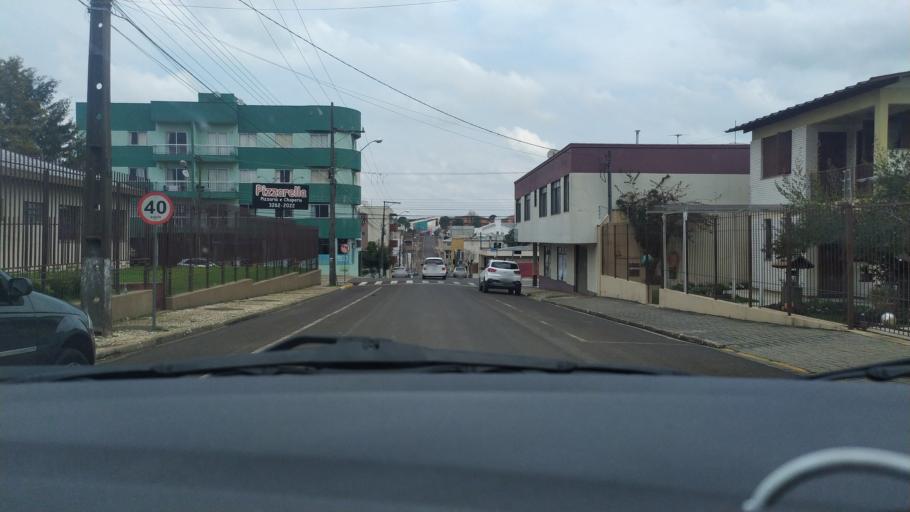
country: BR
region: Parana
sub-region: Palmas
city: Palmas
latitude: -26.4843
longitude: -51.9881
